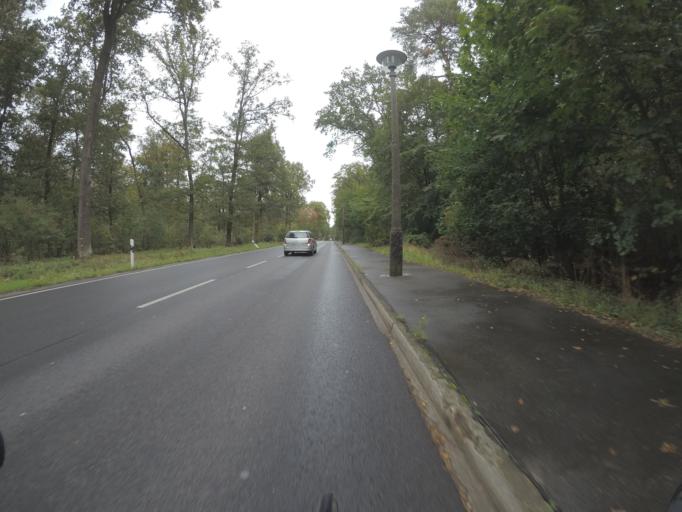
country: DE
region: Berlin
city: Buch
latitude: 52.6414
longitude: 13.4770
